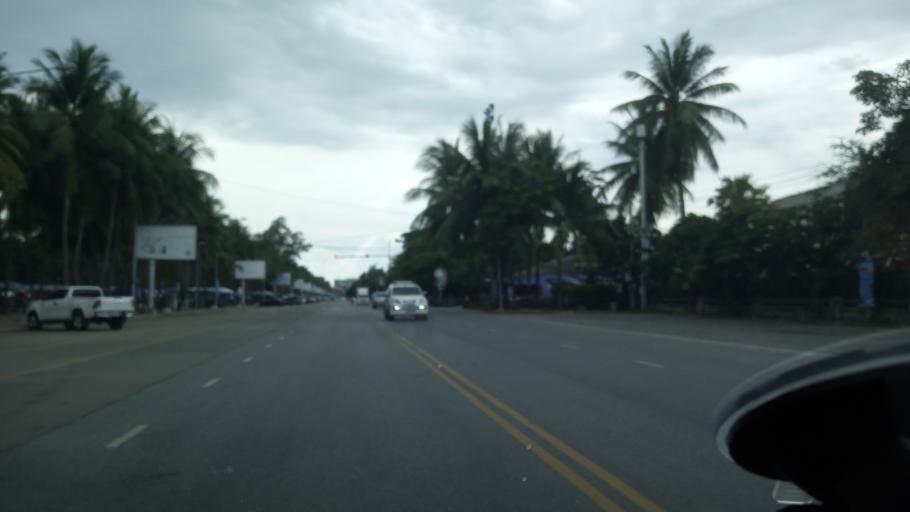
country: TH
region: Chon Buri
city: Chon Buri
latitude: 13.2936
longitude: 100.9073
